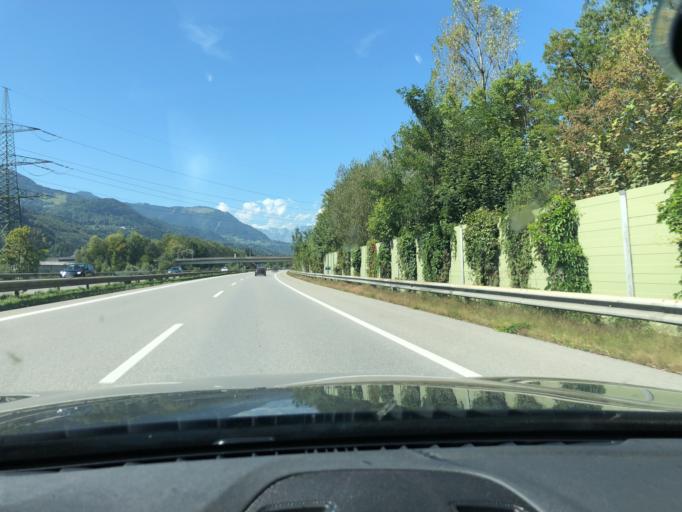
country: AT
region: Vorarlberg
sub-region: Politischer Bezirk Feldkirch
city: Schlins
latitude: 47.1967
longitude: 9.6962
